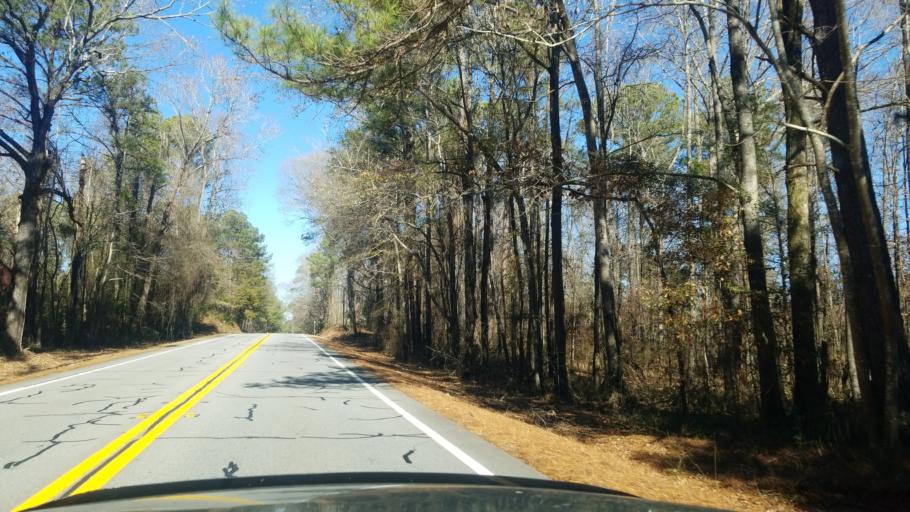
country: US
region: Georgia
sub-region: Harris County
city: Hamilton
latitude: 32.6738
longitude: -84.8591
